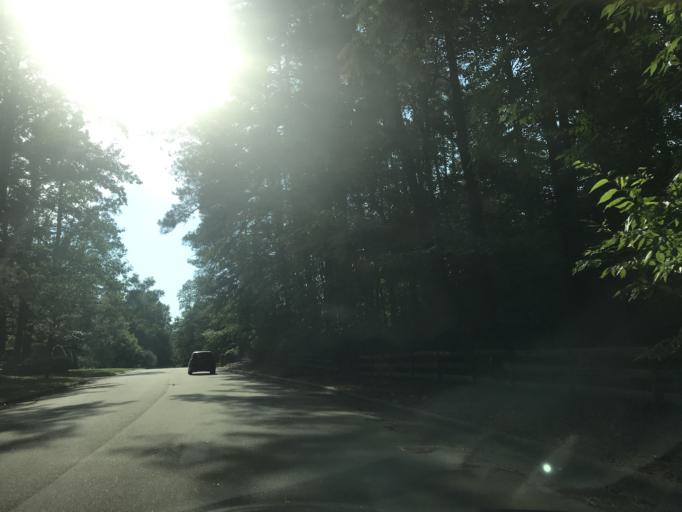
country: US
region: North Carolina
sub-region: Wake County
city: Knightdale
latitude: 35.8307
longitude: -78.5494
